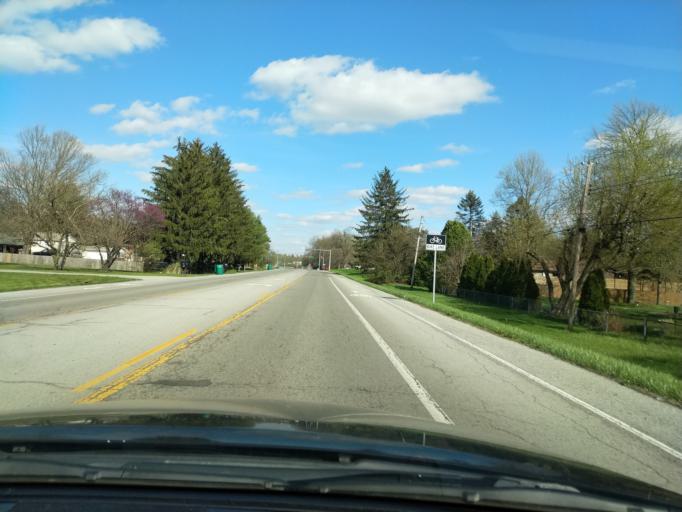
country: US
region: Indiana
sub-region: Marion County
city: Meridian Hills
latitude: 39.8852
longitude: -86.1914
